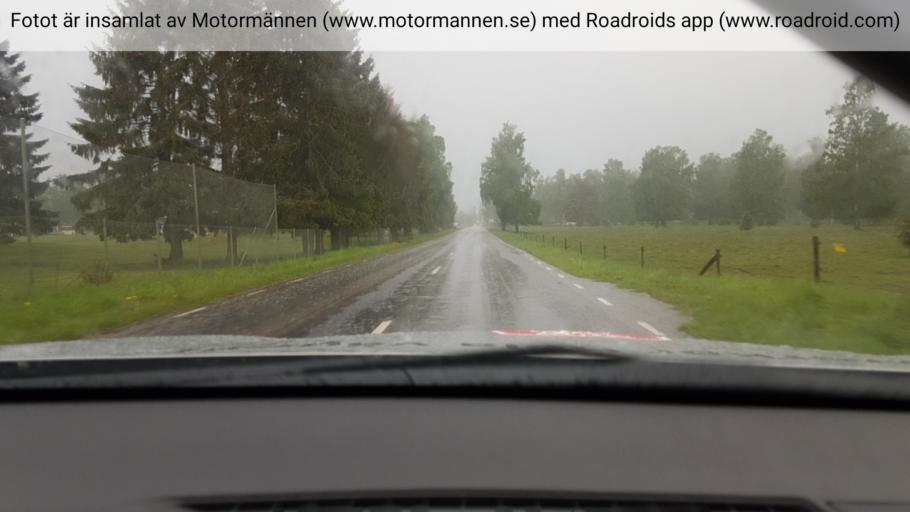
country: SE
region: Vaestra Goetaland
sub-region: Skara Kommun
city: Axvall
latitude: 58.3971
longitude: 13.5806
